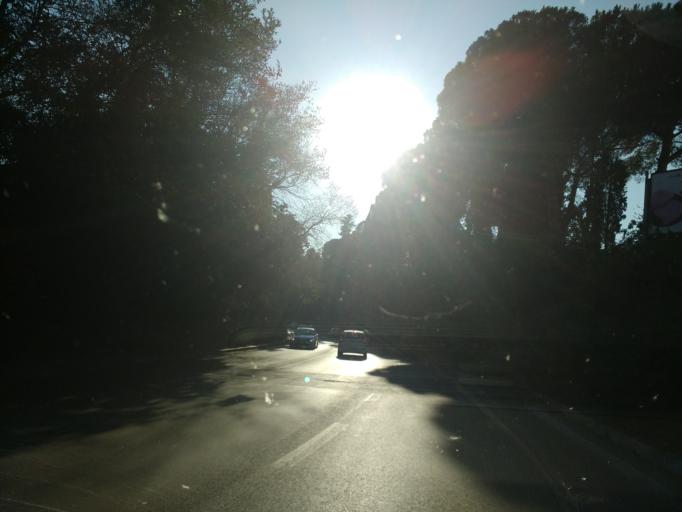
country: IT
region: Latium
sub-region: Citta metropolitana di Roma Capitale
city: Villanova
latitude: 41.9568
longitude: 12.7613
